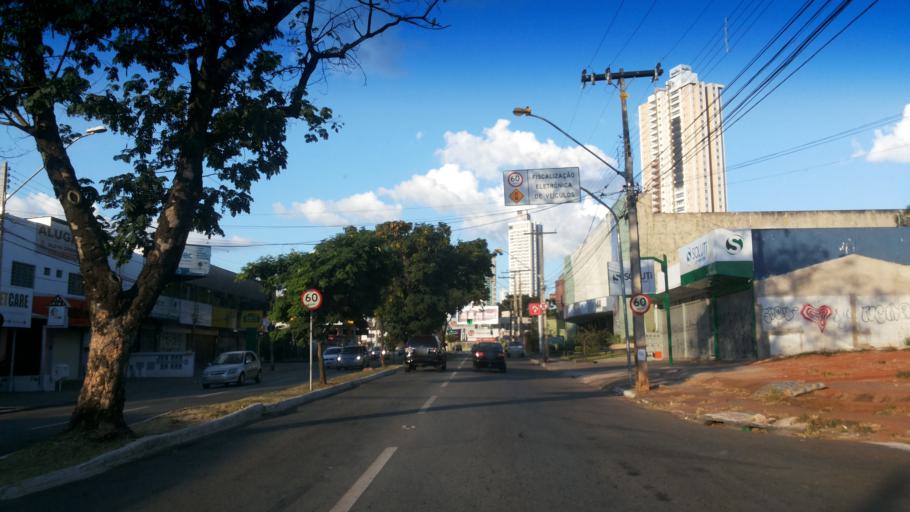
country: BR
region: Goias
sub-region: Goiania
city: Goiania
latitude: -16.7076
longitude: -49.2810
